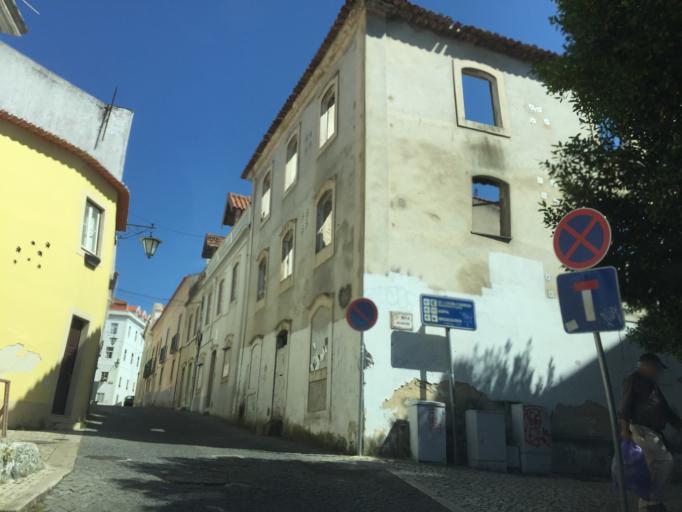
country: PT
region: Leiria
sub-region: Caldas da Rainha
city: Caldas da Rainha
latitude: 39.4026
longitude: -9.1324
